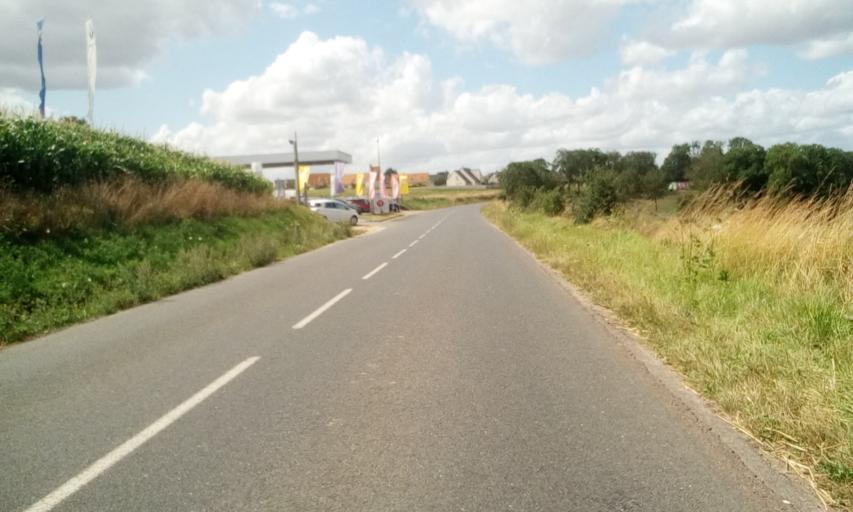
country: FR
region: Lower Normandy
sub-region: Departement du Calvados
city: Creully
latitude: 49.2823
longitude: -0.5282
